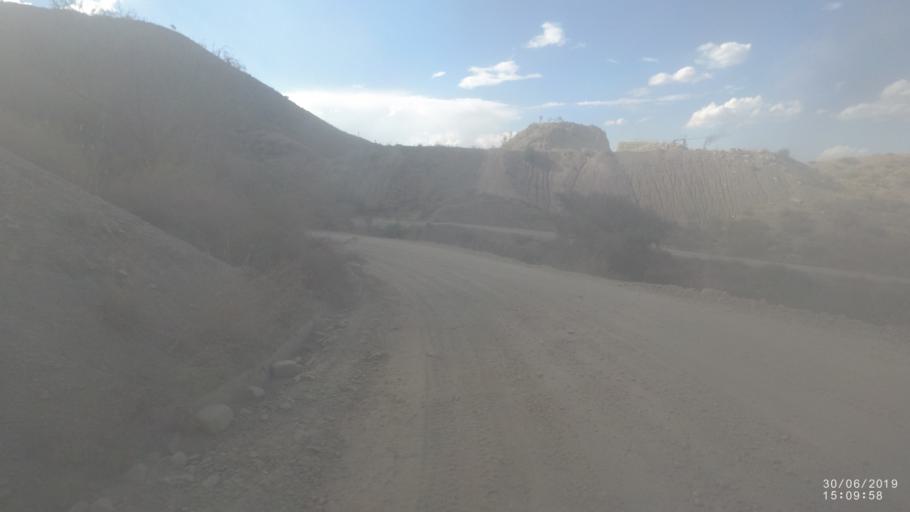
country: BO
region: Cochabamba
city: Irpa Irpa
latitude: -17.7287
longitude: -66.2972
